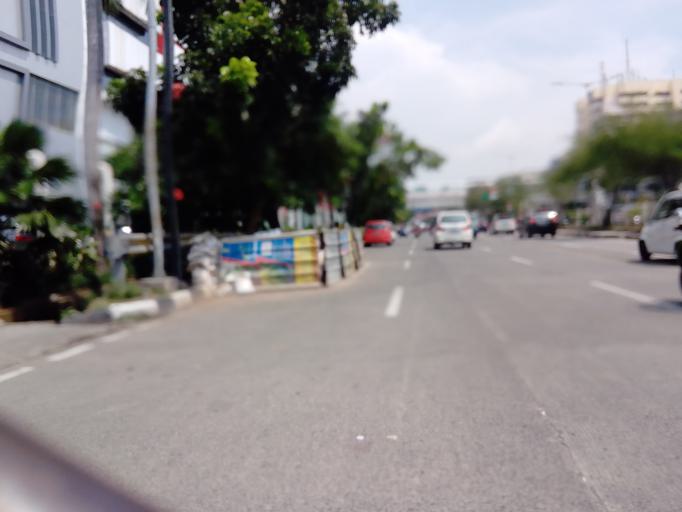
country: ID
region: Jakarta Raya
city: Jakarta
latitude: -6.1361
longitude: 106.8276
